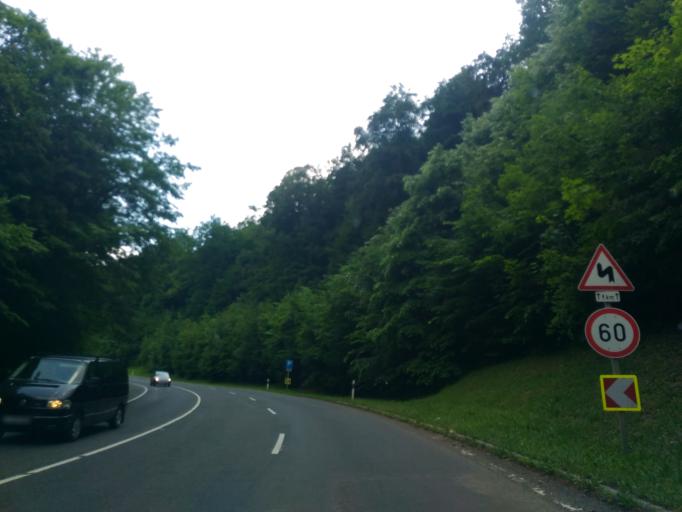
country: HU
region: Baranya
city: Komlo
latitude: 46.1482
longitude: 18.2432
